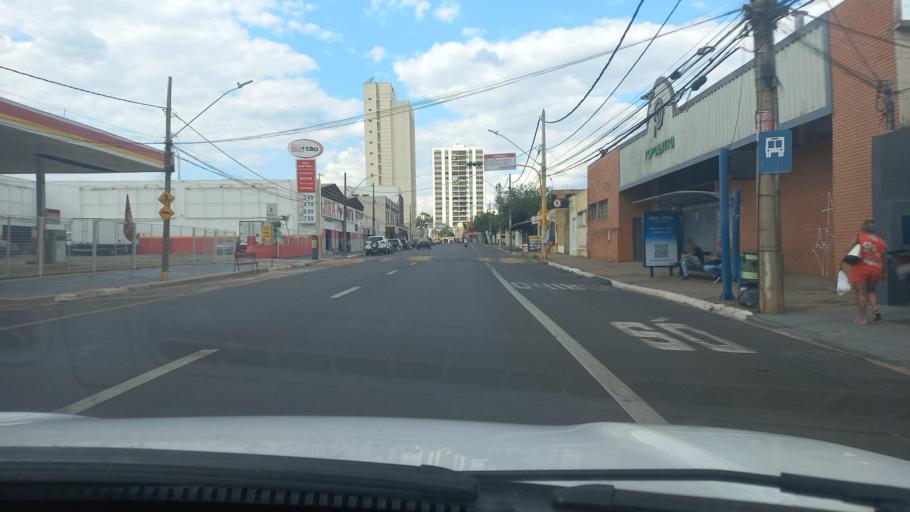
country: BR
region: Minas Gerais
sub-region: Uberaba
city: Uberaba
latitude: -19.7455
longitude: -47.9335
